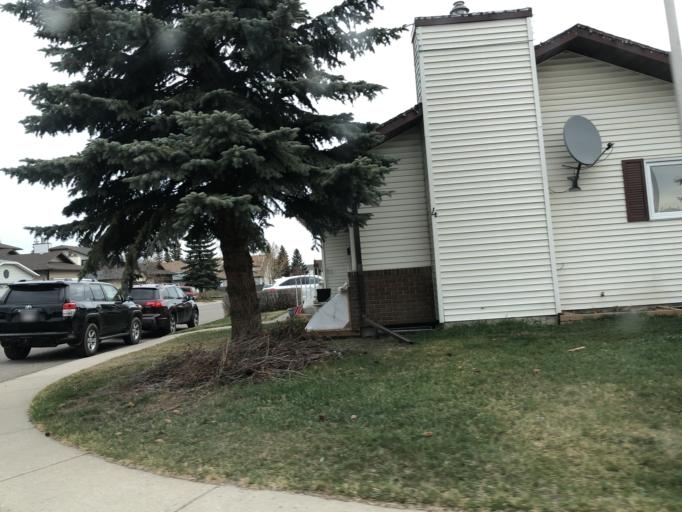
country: CA
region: Alberta
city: Calgary
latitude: 51.0719
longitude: -114.0119
